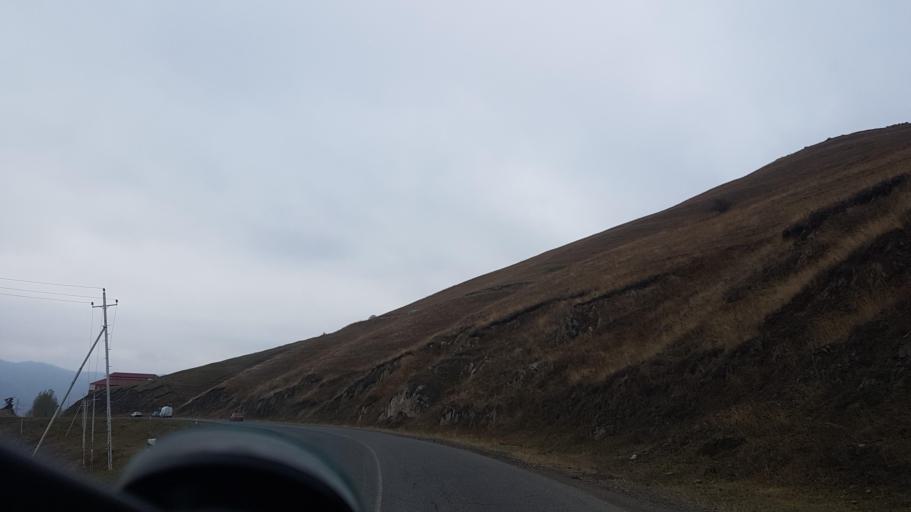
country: AZ
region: Gadabay Rayon
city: Ariqdam
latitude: 40.6167
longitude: 45.8102
